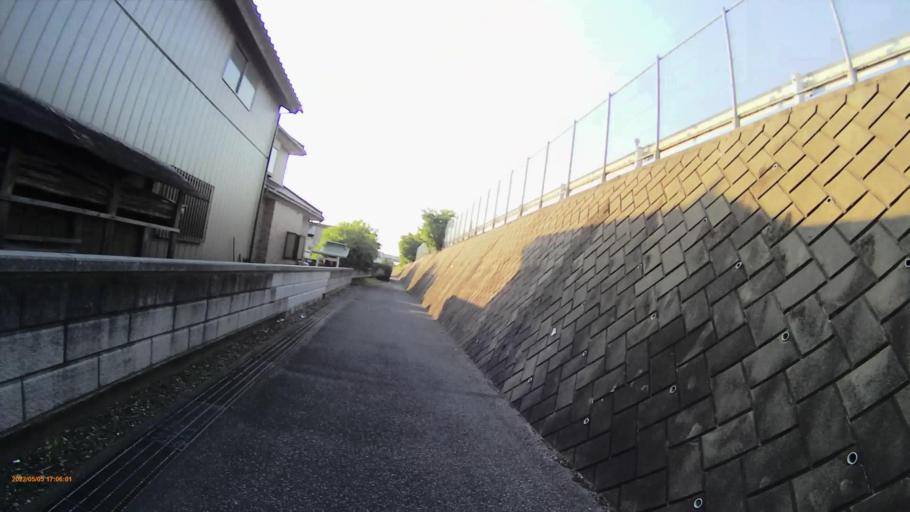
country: JP
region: Saitama
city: Kurihashi
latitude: 36.1210
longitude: 139.7170
